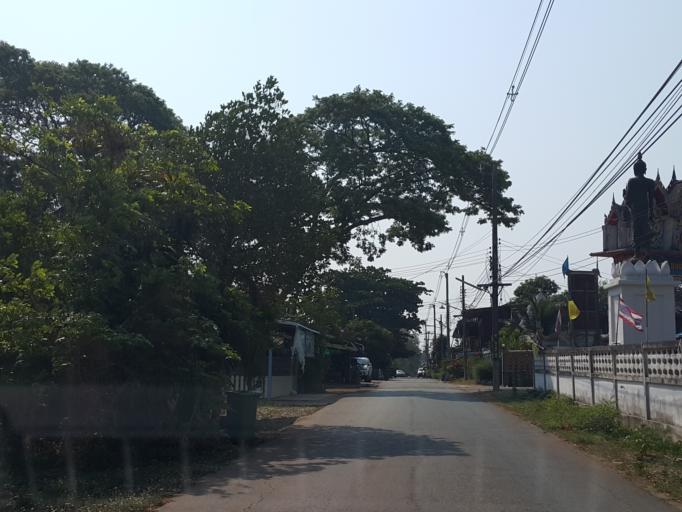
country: TH
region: Kanchanaburi
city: Sai Yok
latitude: 14.1203
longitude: 99.1373
